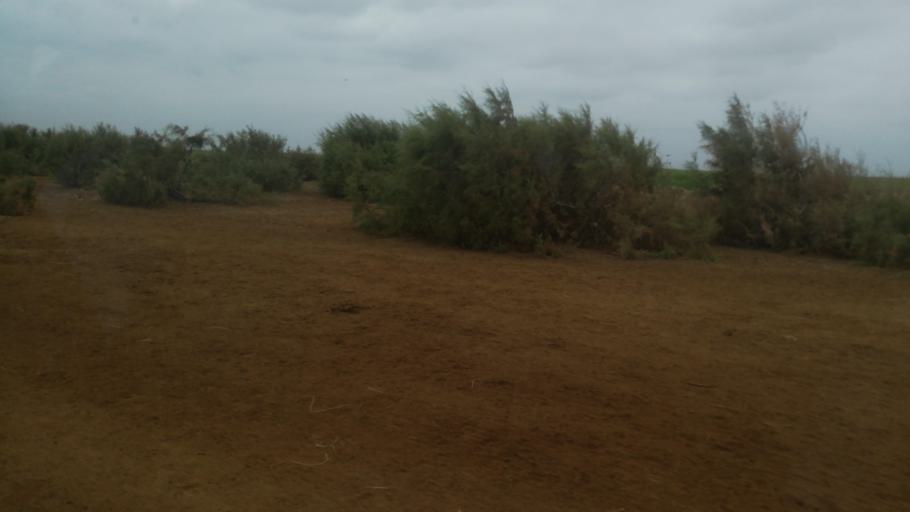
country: SN
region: Saint-Louis
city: Saint-Louis
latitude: 16.3154
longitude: -16.2313
